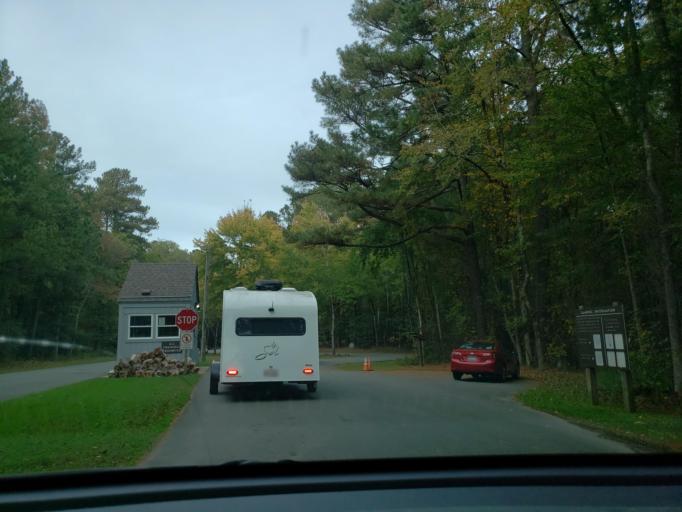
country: US
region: North Carolina
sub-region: Chatham County
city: Fearrington Village
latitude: 35.7412
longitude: -79.0391
